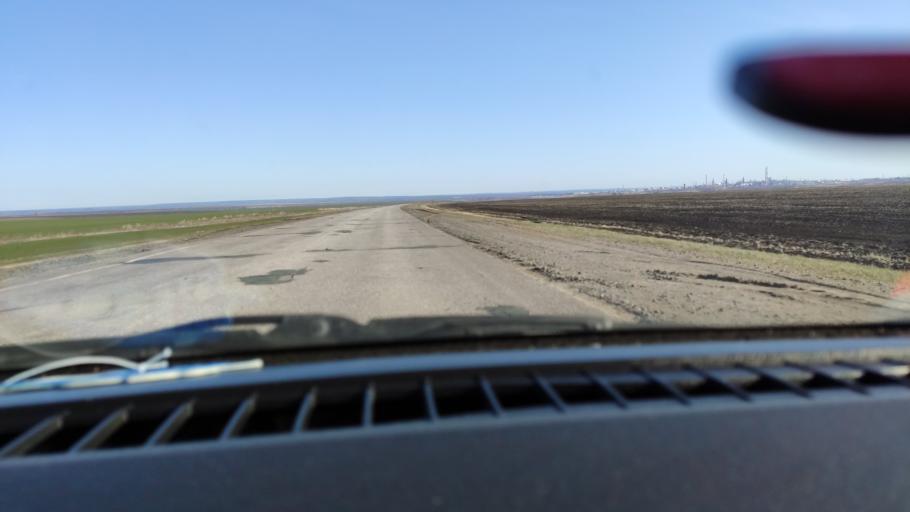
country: RU
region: Samara
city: Varlamovo
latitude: 53.0253
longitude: 48.3337
